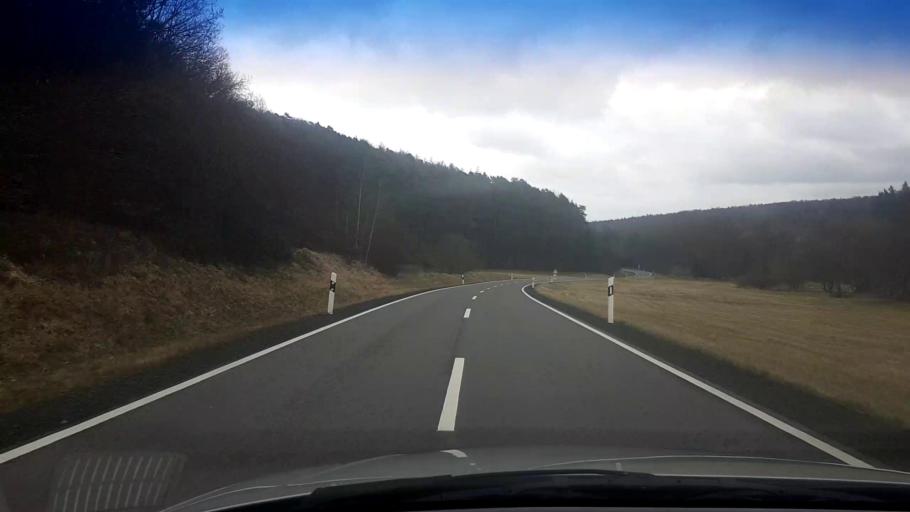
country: DE
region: Bavaria
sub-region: Regierungsbezirk Unterfranken
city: Sand
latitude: 49.9415
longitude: 10.6163
